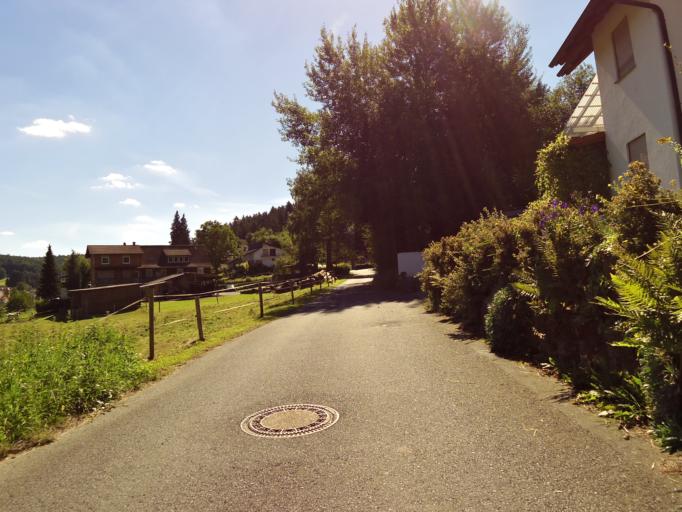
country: DE
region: Hesse
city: Reichelsheim
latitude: 49.6384
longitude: 8.8988
